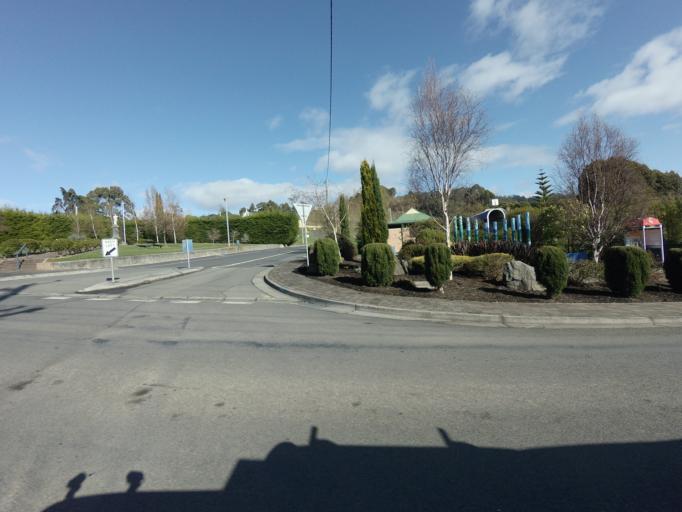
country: AU
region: Tasmania
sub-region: Huon Valley
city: Cygnet
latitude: -43.3131
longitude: 147.0155
